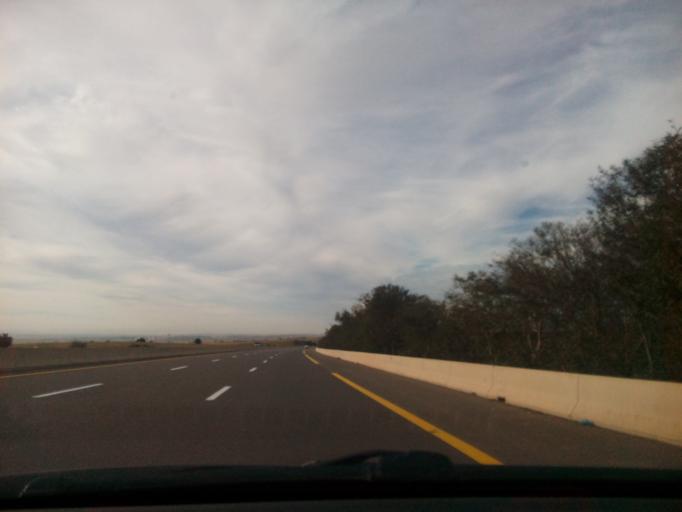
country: DZ
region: Sidi Bel Abbes
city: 'Ain el Berd
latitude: 35.3332
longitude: -0.5235
